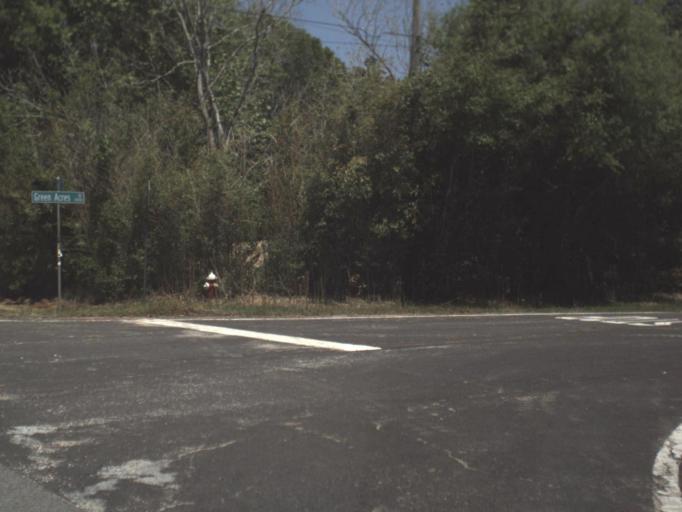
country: US
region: Florida
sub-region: Escambia County
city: Bellview
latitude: 30.4651
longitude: -87.3241
